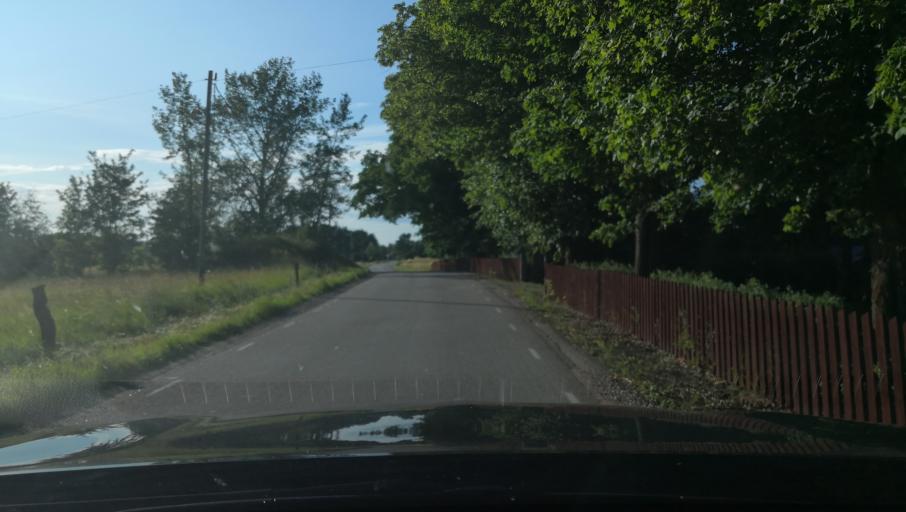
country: SE
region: Uppsala
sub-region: Uppsala Kommun
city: Vattholma
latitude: 59.9273
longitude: 17.8372
